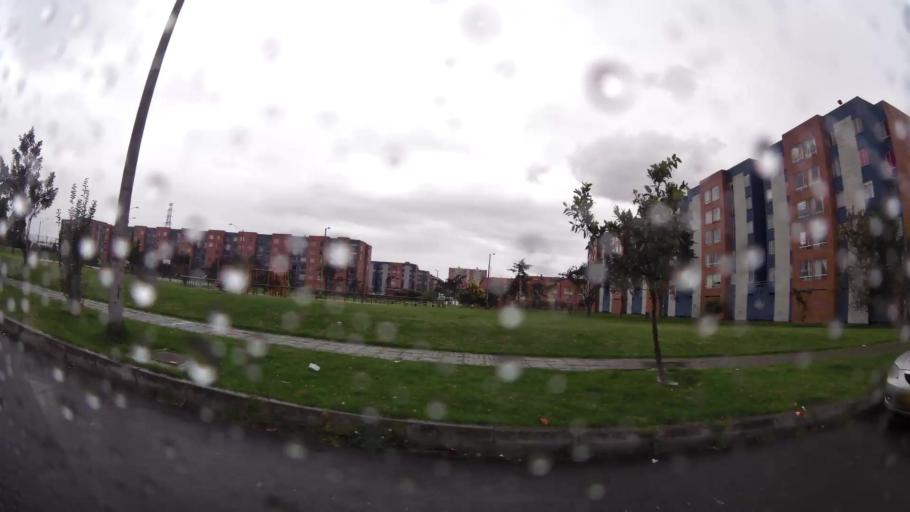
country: CO
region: Bogota D.C.
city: Bogota
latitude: 4.6628
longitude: -74.1278
